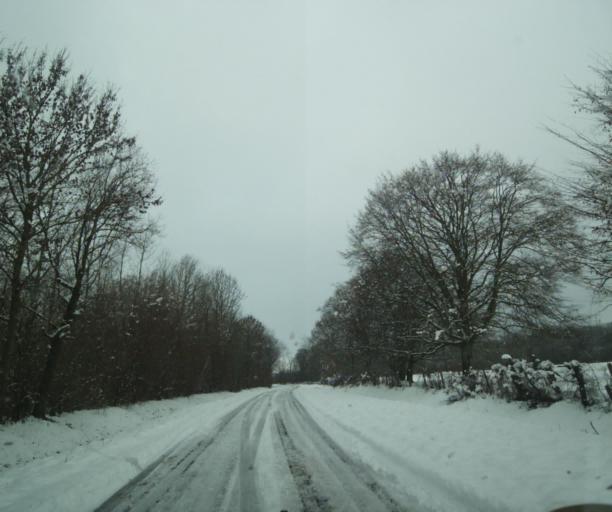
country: FR
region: Champagne-Ardenne
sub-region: Departement de la Haute-Marne
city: Montier-en-Der
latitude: 48.4824
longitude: 4.6804
